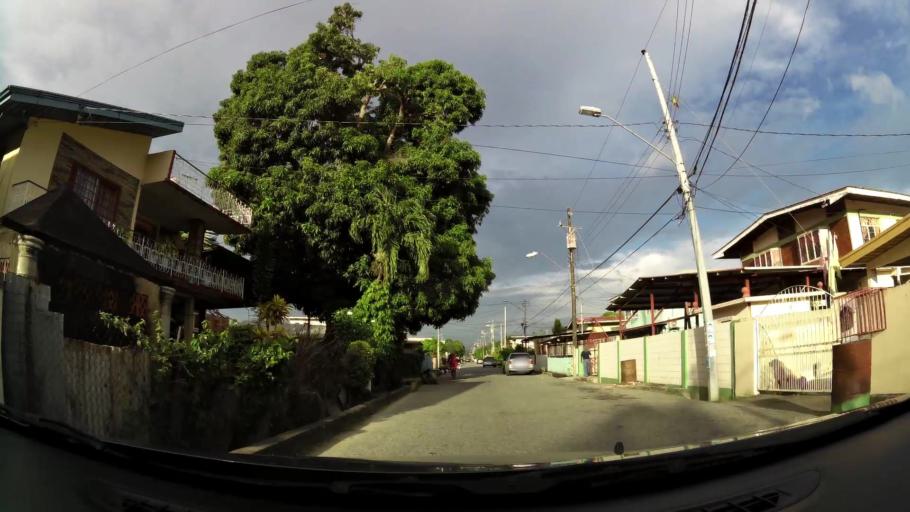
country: TT
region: Tunapuna/Piarco
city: Tunapuna
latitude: 10.6423
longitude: -61.4031
